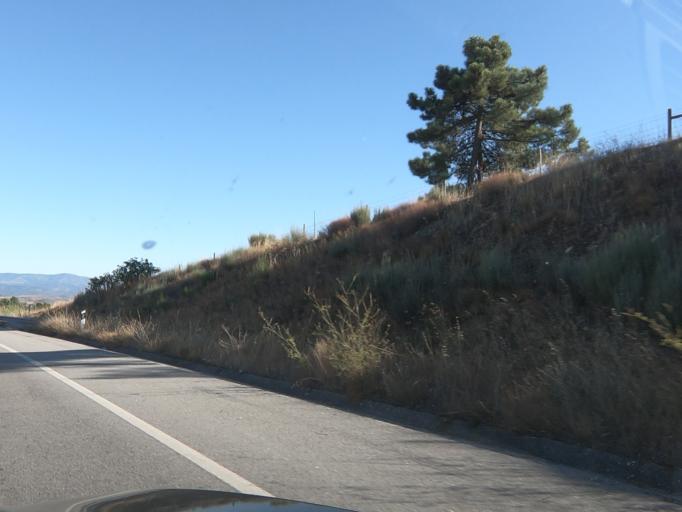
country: PT
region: Vila Real
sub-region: Valpacos
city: Valpacos
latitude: 41.5715
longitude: -7.2973
